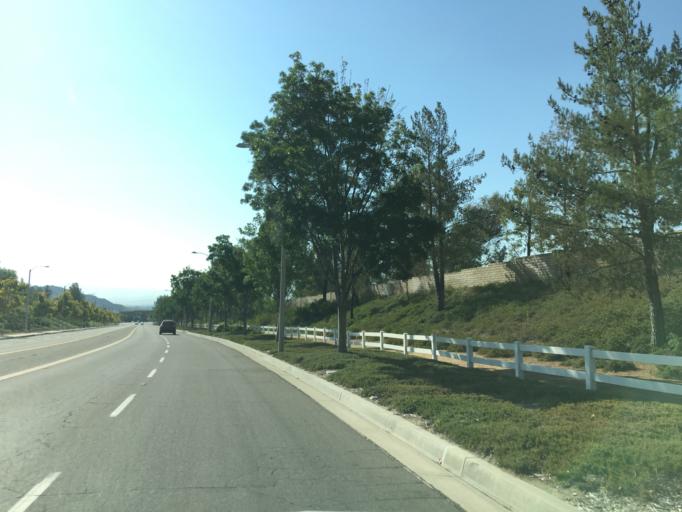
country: US
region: California
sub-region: Los Angeles County
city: Valencia
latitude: 34.4526
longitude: -118.6305
